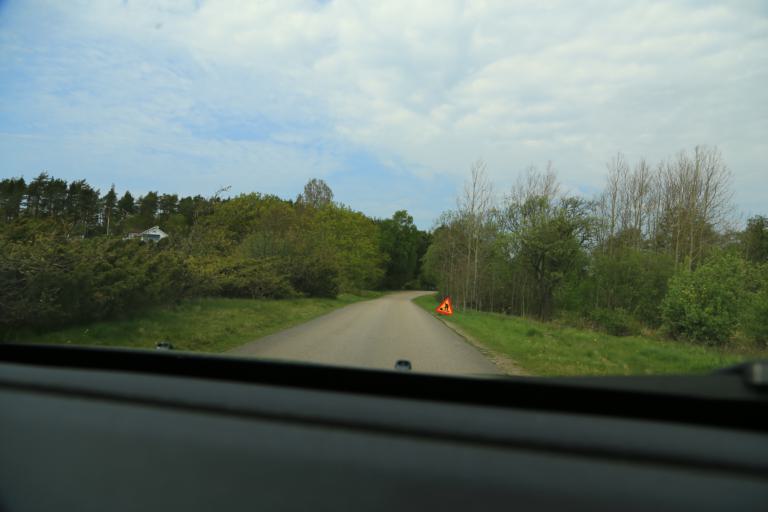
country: SE
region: Halland
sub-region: Varbergs Kommun
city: Varberg
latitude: 57.1434
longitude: 12.2274
